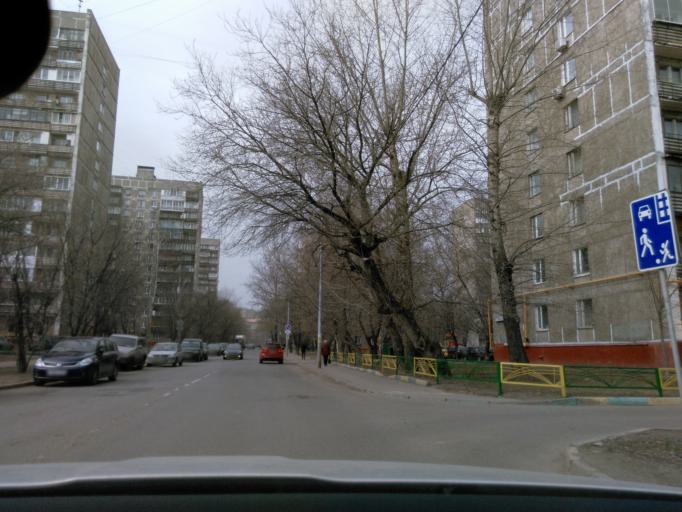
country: RU
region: Moskovskaya
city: Koptevo
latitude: 55.8189
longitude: 37.5175
